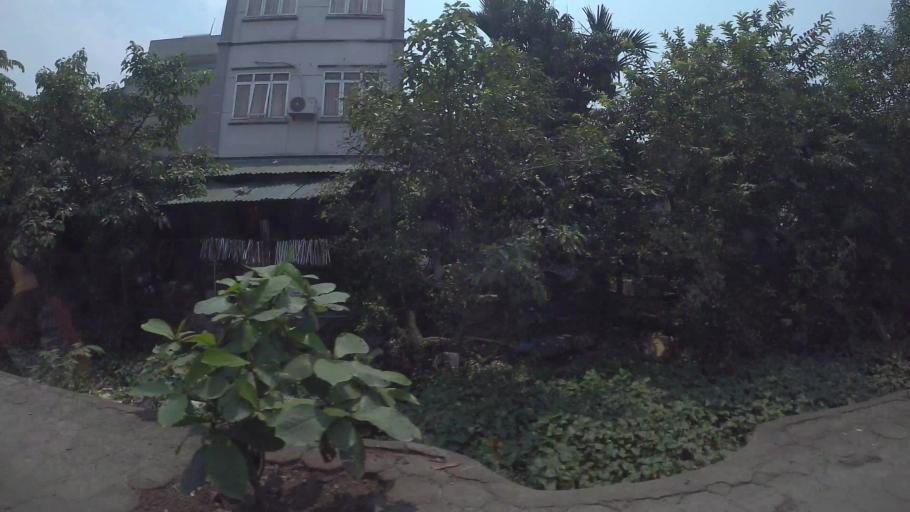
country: VN
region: Ha Noi
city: Van Dien
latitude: 20.9556
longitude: 105.8304
